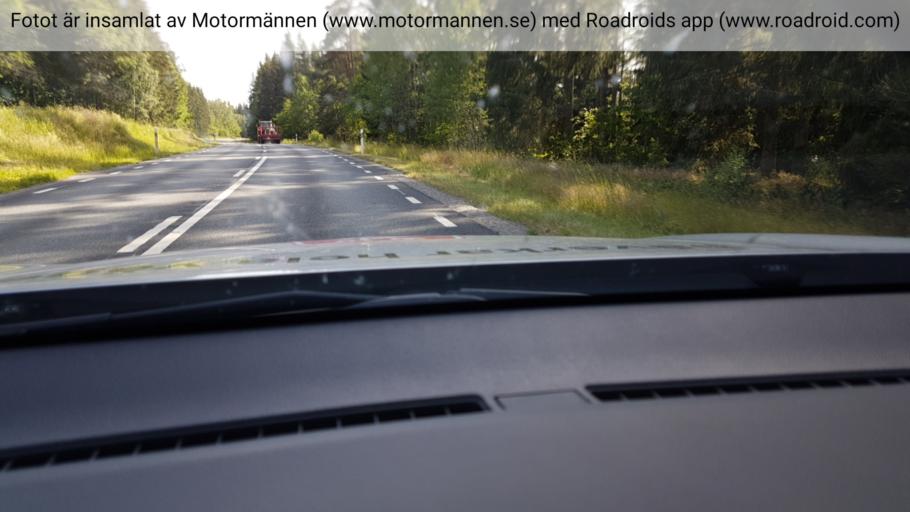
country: SE
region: Joenkoeping
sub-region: Aneby Kommun
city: Aneby
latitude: 57.9044
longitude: 14.8936
